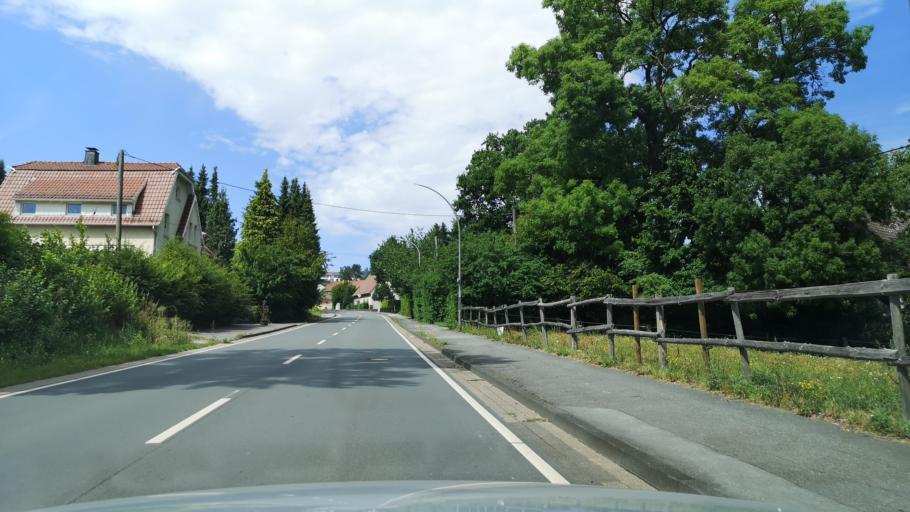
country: DE
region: North Rhine-Westphalia
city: Hemer
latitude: 51.4001
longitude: 7.7553
